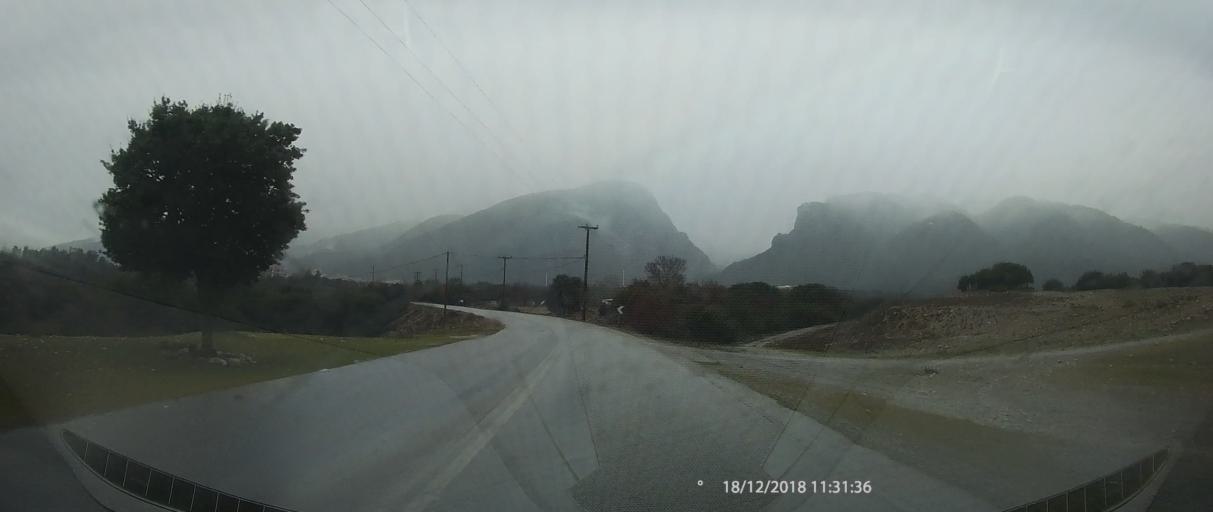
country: GR
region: Central Macedonia
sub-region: Nomos Pierias
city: Litochoro
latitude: 40.1129
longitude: 22.5088
